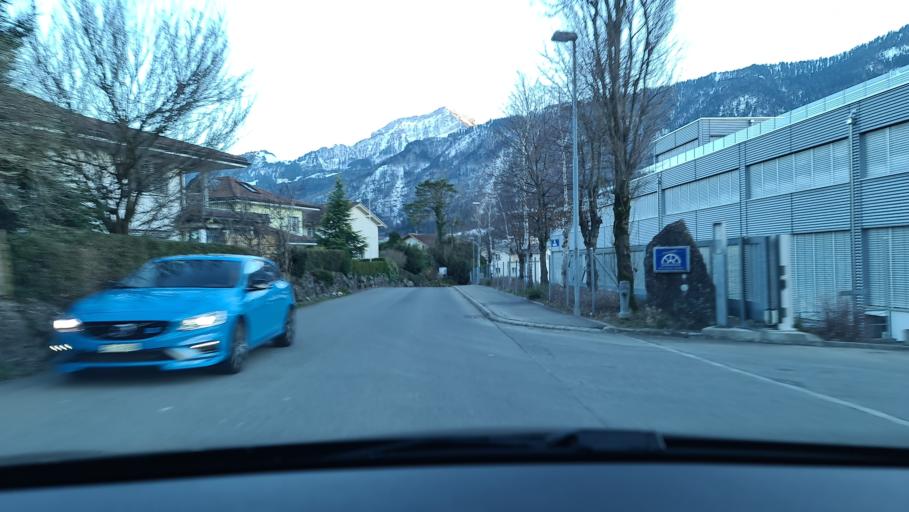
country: CH
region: Schwyz
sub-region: Bezirk Schwyz
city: Goldau
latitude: 47.0552
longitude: 8.5506
